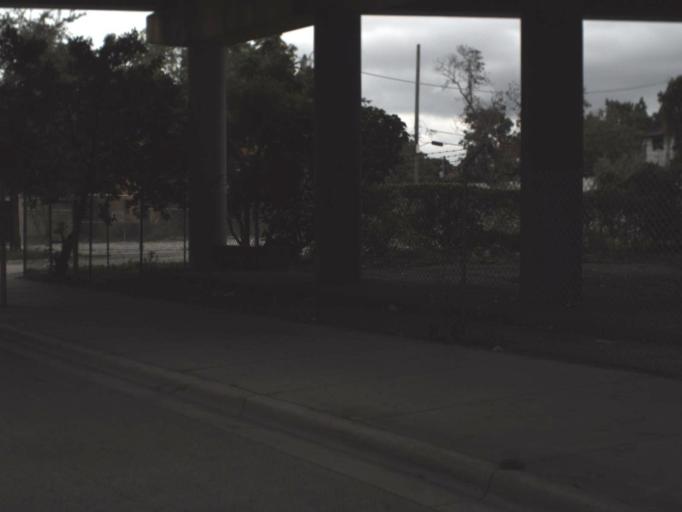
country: US
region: Florida
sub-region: Miami-Dade County
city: Miami
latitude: 25.7885
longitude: -80.1999
